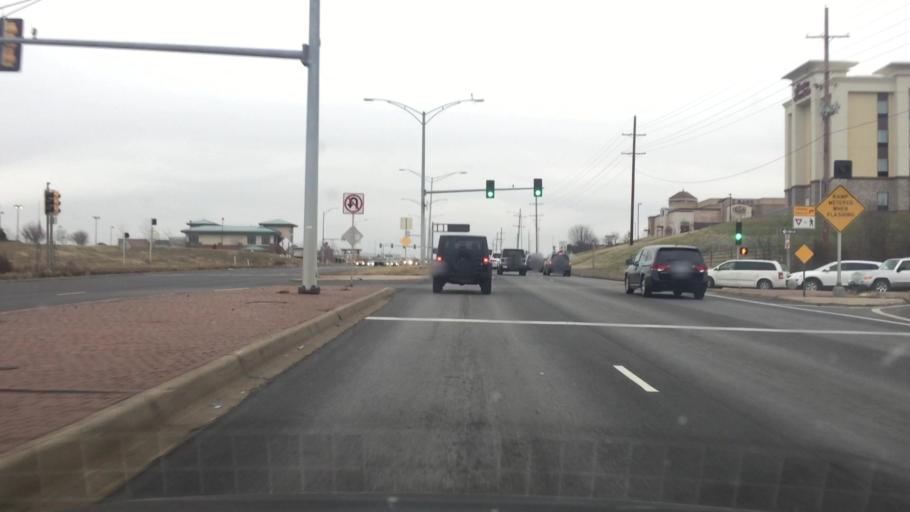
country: US
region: Kansas
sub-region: Johnson County
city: Lenexa
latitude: 38.8837
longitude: -94.6750
